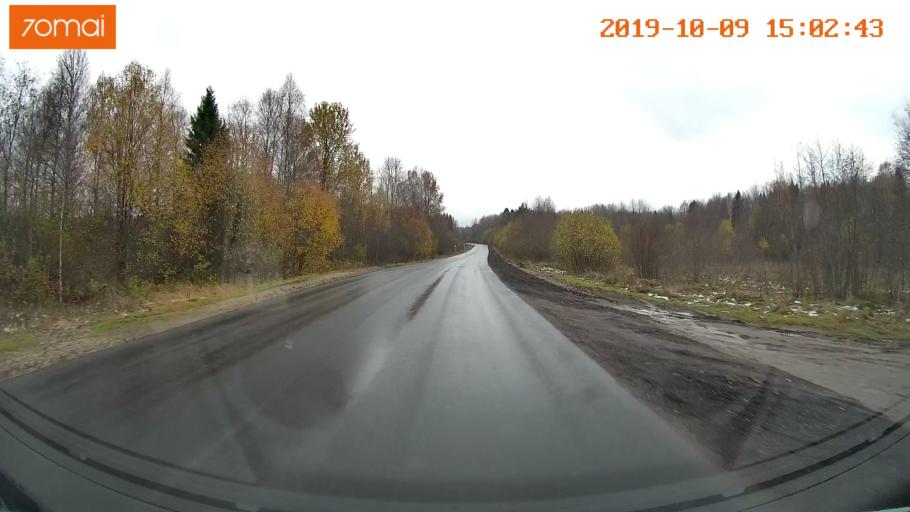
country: RU
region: Kostroma
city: Chistyye Bory
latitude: 58.2812
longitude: 41.6776
